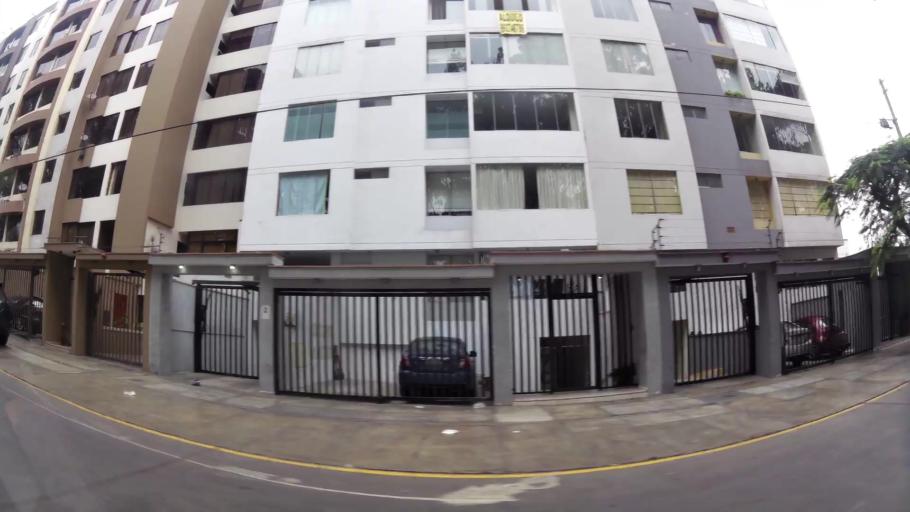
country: PE
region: Lima
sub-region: Lima
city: San Luis
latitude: -12.0942
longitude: -76.9999
